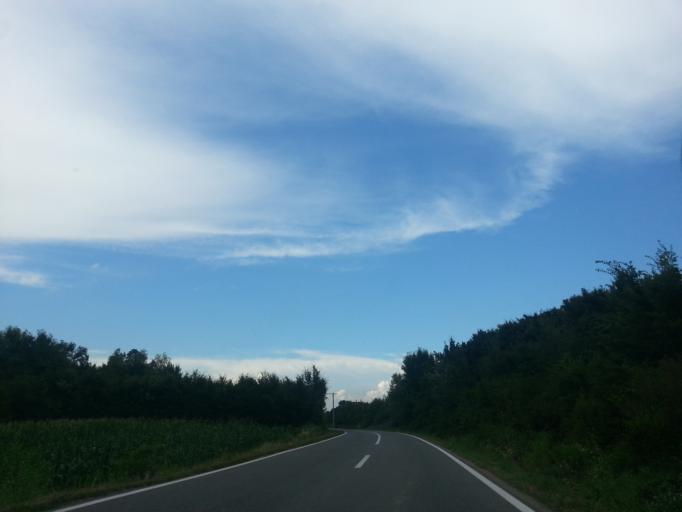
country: BA
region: Brcko
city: Brcko
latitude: 44.7869
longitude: 18.8166
